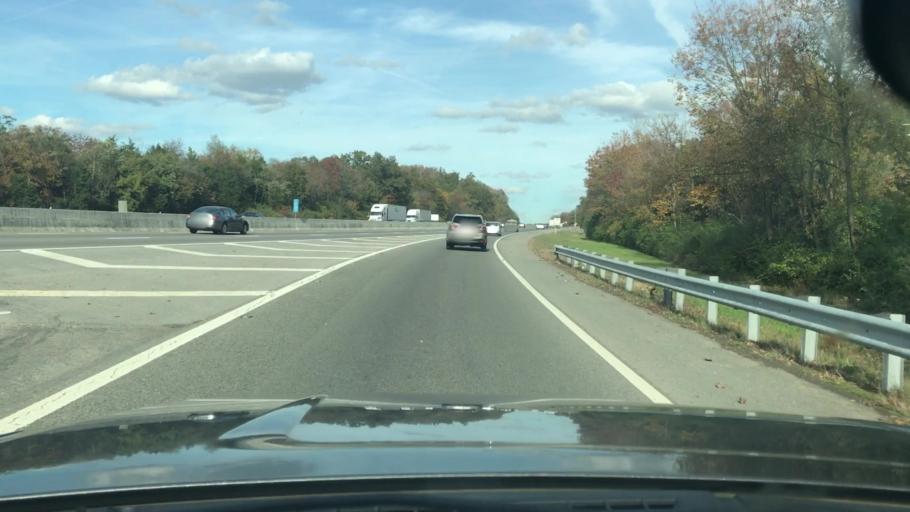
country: US
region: Tennessee
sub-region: Davidson County
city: Belle Meade
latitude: 36.1124
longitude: -86.9209
